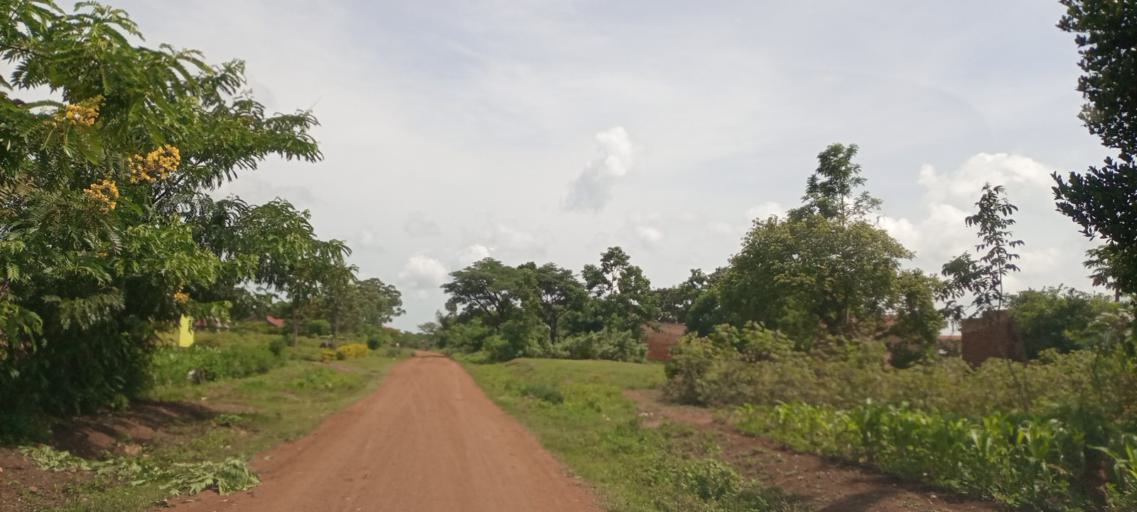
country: UG
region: Eastern Region
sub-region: Budaka District
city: Budaka
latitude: 1.1745
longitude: 33.9267
